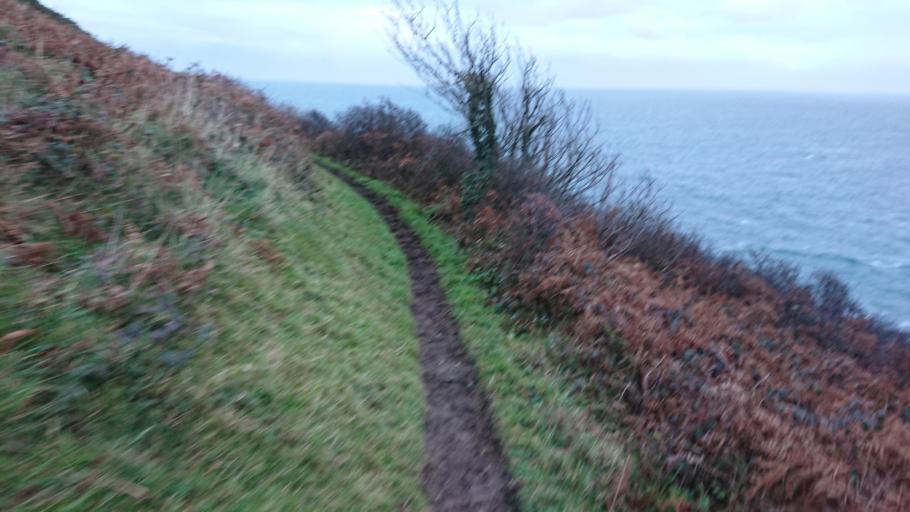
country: GB
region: England
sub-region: Cornwall
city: Fowey
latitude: 50.3296
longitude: -4.5680
